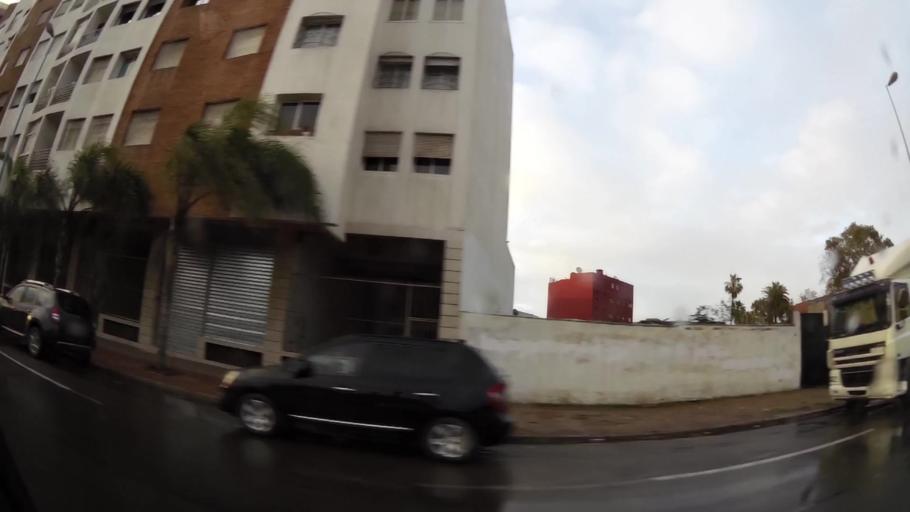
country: MA
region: Grand Casablanca
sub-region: Casablanca
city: Casablanca
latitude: 33.5866
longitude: -7.5869
